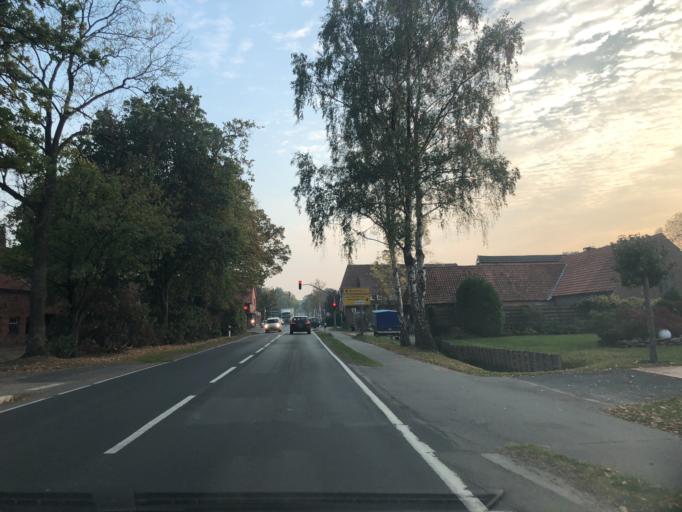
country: DE
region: Lower Saxony
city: Wardenburg
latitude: 53.0716
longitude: 8.1650
